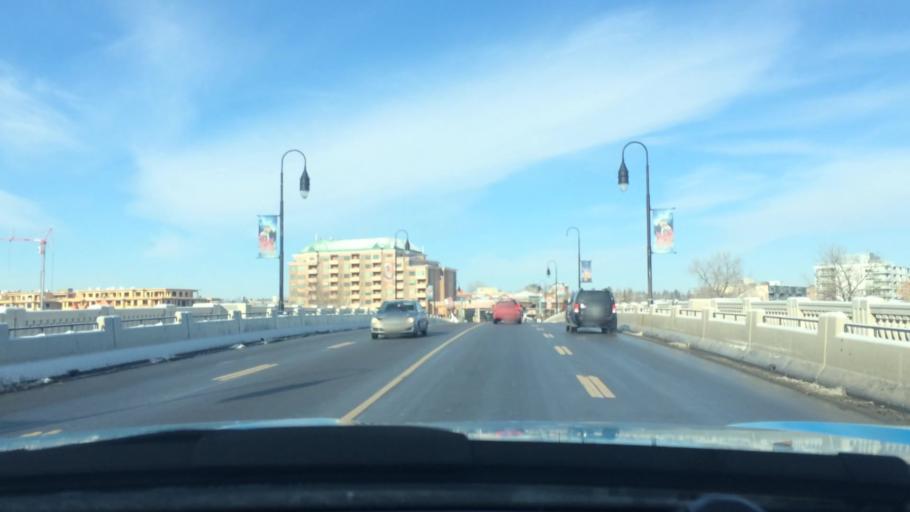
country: CA
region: Alberta
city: Calgary
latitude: 51.0504
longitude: -114.0840
